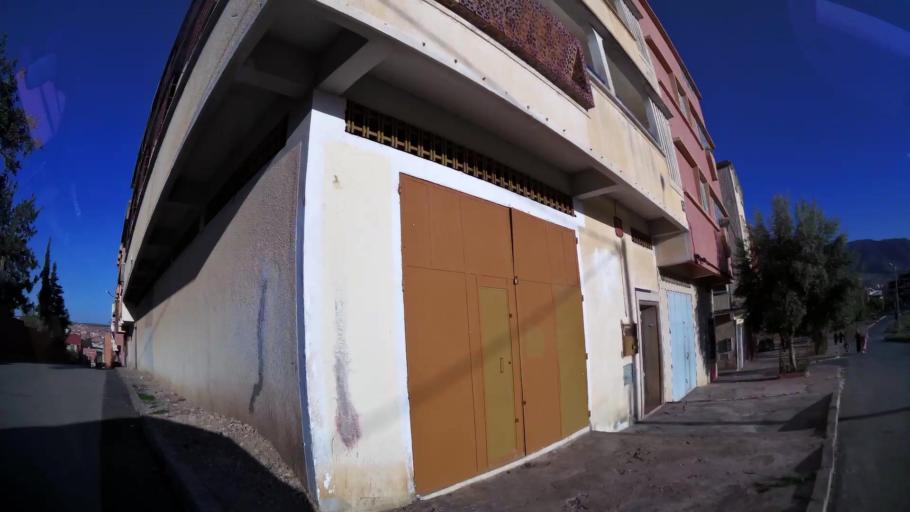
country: MA
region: Oriental
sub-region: Berkane-Taourirt
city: Berkane
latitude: 34.9264
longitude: -2.3220
